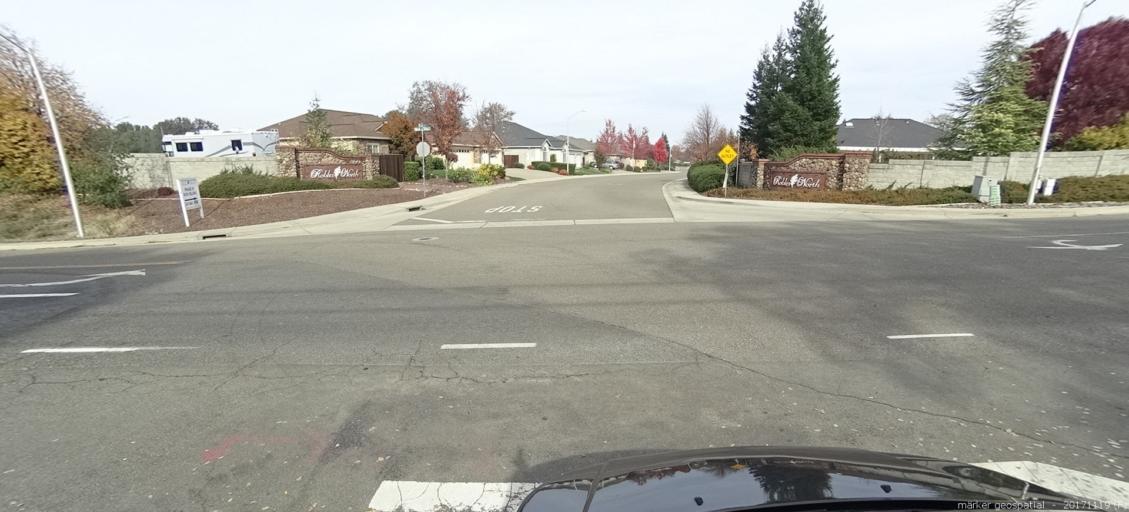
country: US
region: California
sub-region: Shasta County
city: Anderson
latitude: 40.4983
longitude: -122.3114
